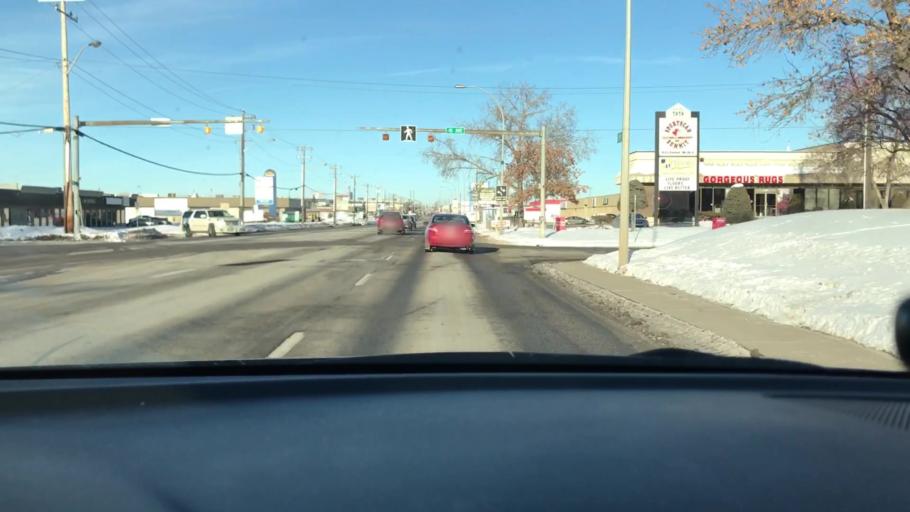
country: CA
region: Alberta
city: Edmonton
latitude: 53.4828
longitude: -113.4861
